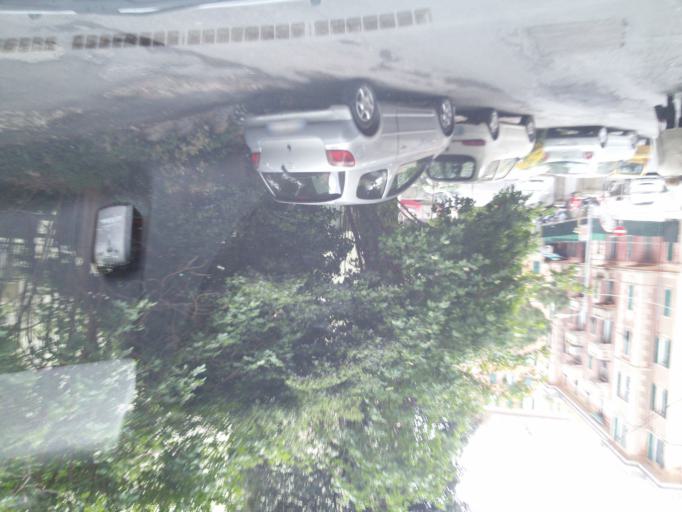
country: IT
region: Liguria
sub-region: Provincia di Genova
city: Genoa
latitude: 44.4042
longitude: 8.9783
